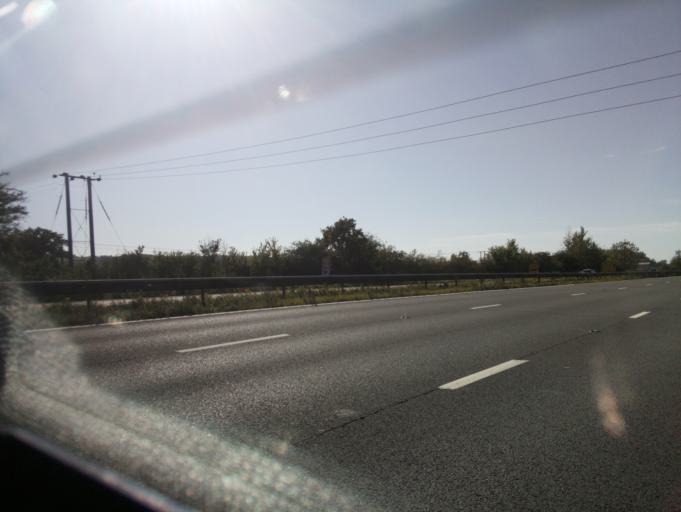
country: GB
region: England
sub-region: Borough of Swindon
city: Wroughton
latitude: 51.5406
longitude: -1.8113
